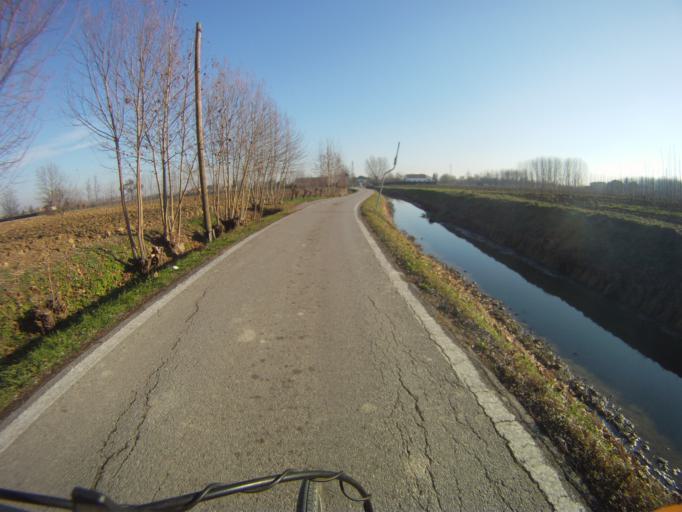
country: IT
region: Veneto
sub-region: Provincia di Padova
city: Campagnola
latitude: 45.2944
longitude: 12.0139
